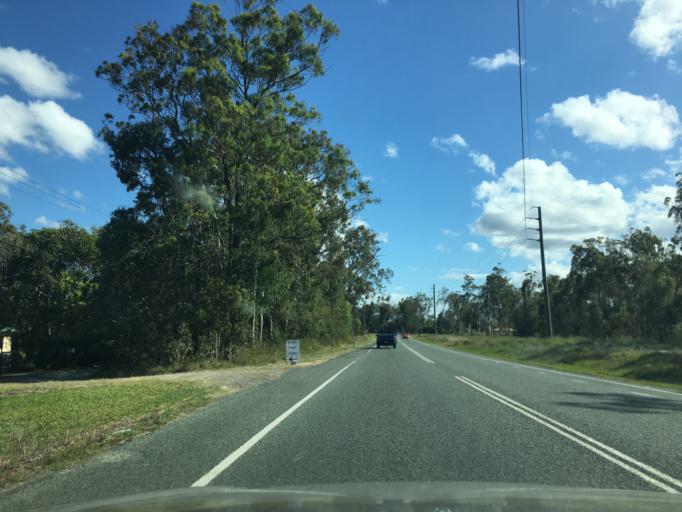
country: AU
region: Queensland
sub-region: Logan
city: Chambers Flat
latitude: -27.7797
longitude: 153.1007
